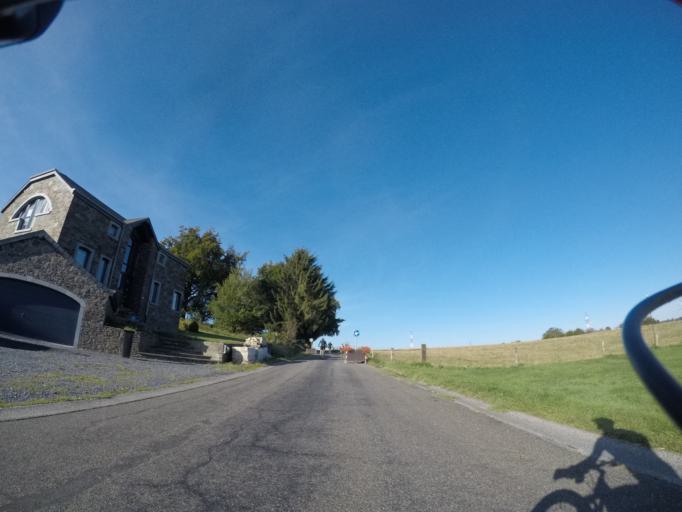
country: BE
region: Wallonia
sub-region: Province du Luxembourg
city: Bastogne
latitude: 49.9653
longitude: 5.6764
